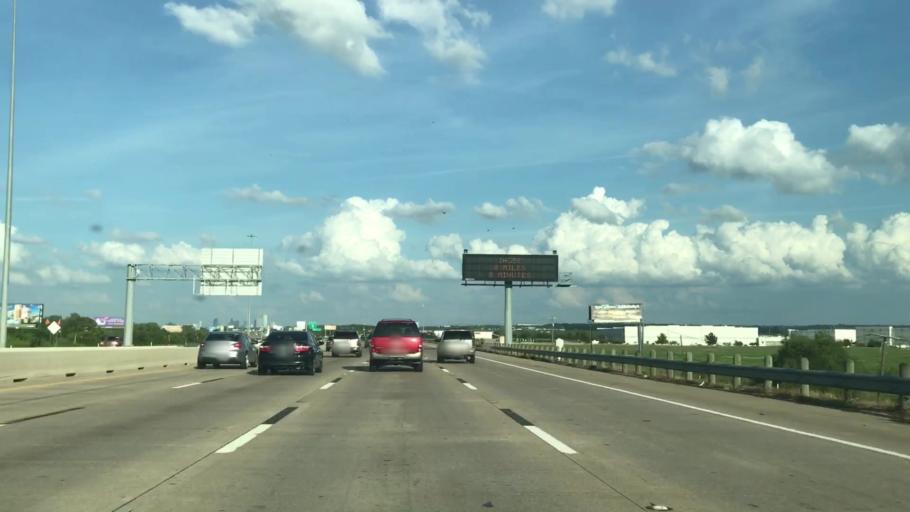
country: US
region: Texas
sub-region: Dallas County
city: Grand Prairie
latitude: 32.7621
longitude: -96.9529
